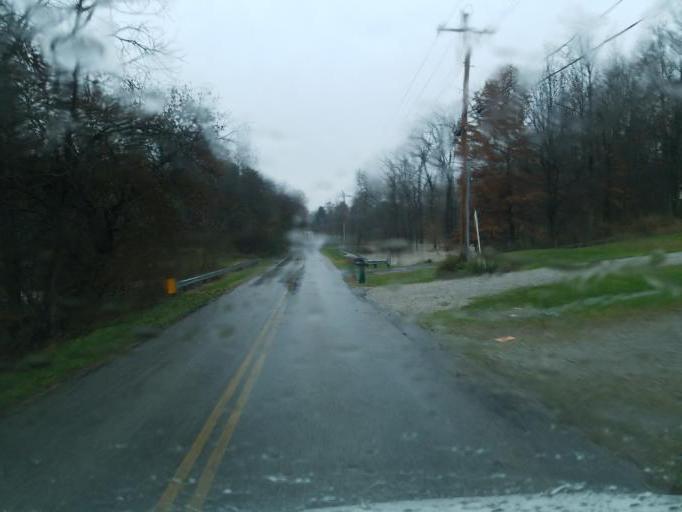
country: US
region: Ohio
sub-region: Delaware County
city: Sunbury
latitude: 40.2887
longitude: -82.8737
